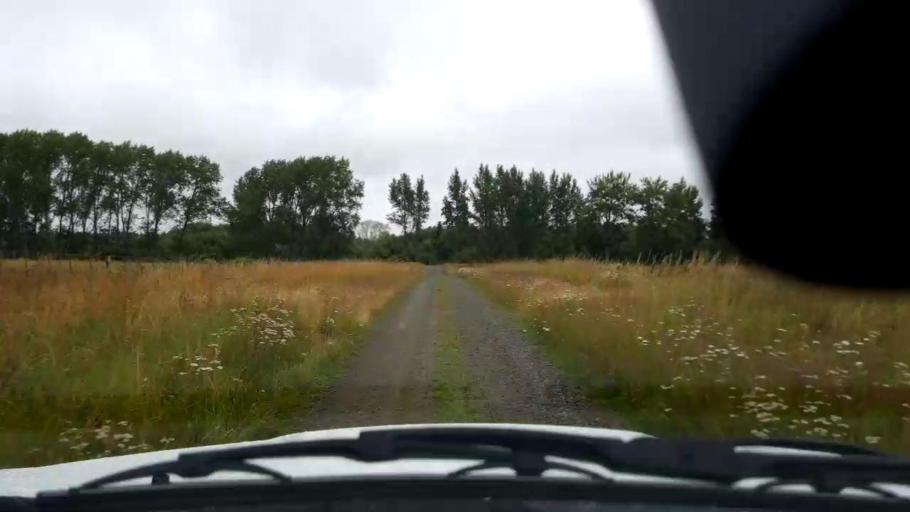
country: NZ
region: Canterbury
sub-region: Timaru District
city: Pleasant Point
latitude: -44.2593
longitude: 171.1986
